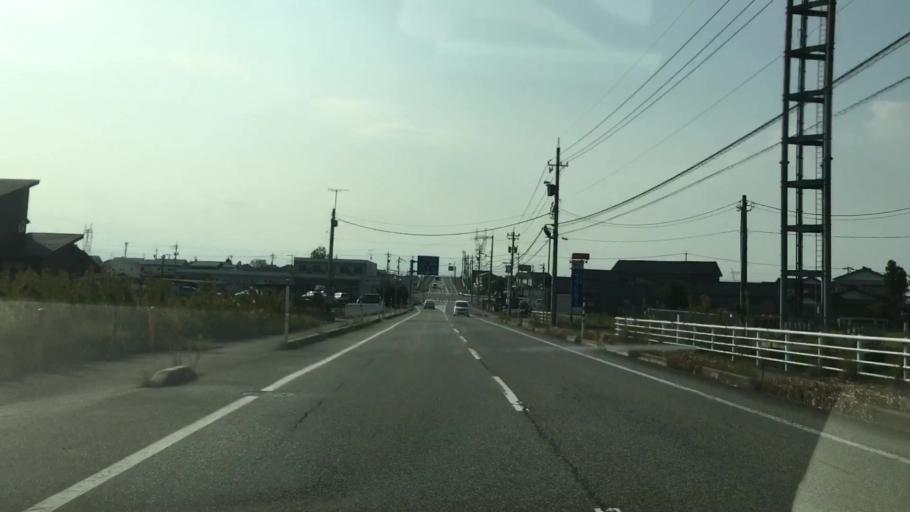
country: JP
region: Toyama
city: Kamiichi
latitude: 36.7050
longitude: 137.3165
